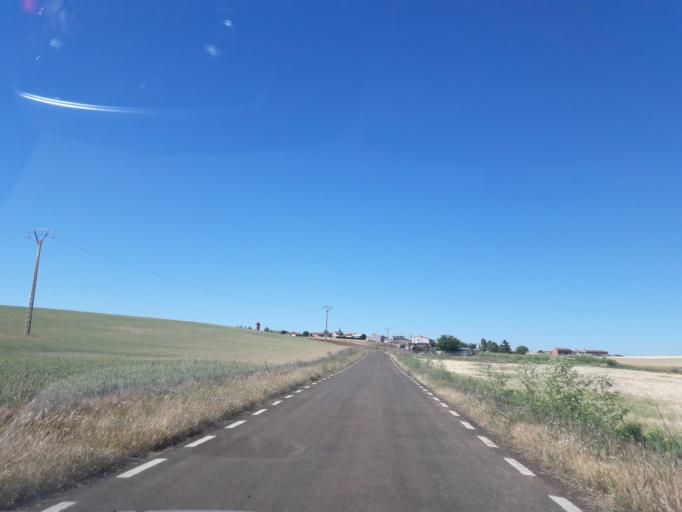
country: ES
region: Castille and Leon
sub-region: Provincia de Salamanca
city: Parada de Arriba
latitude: 40.9921
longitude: -5.7900
